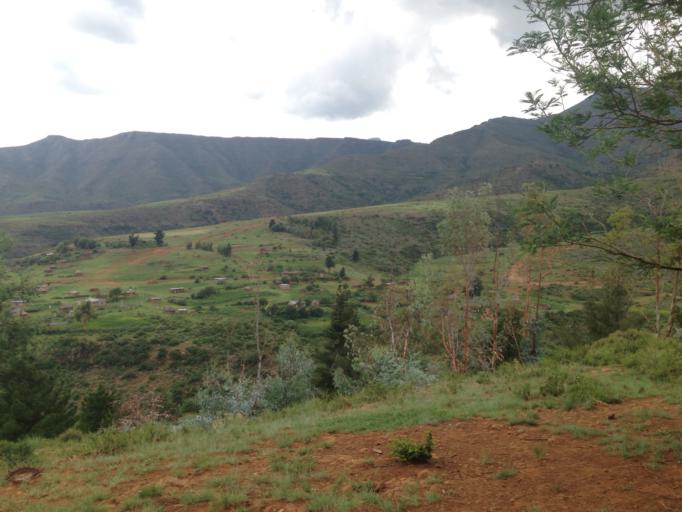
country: LS
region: Maseru
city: Nako
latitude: -29.5897
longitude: 27.7595
